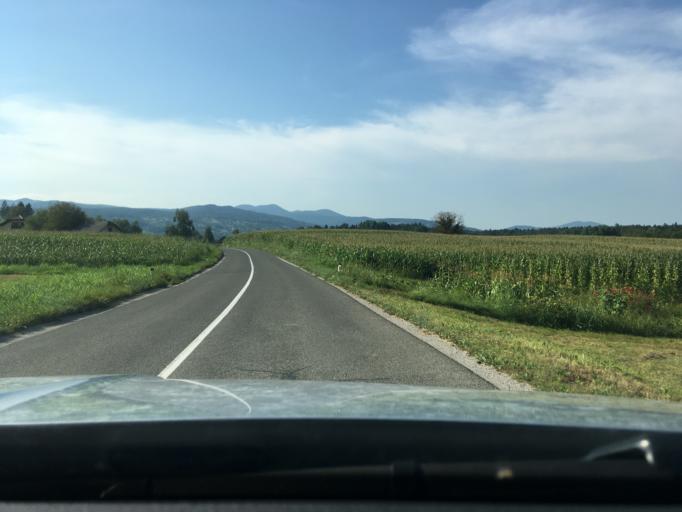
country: SI
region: Crnomelj
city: Crnomelj
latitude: 45.5363
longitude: 15.1634
